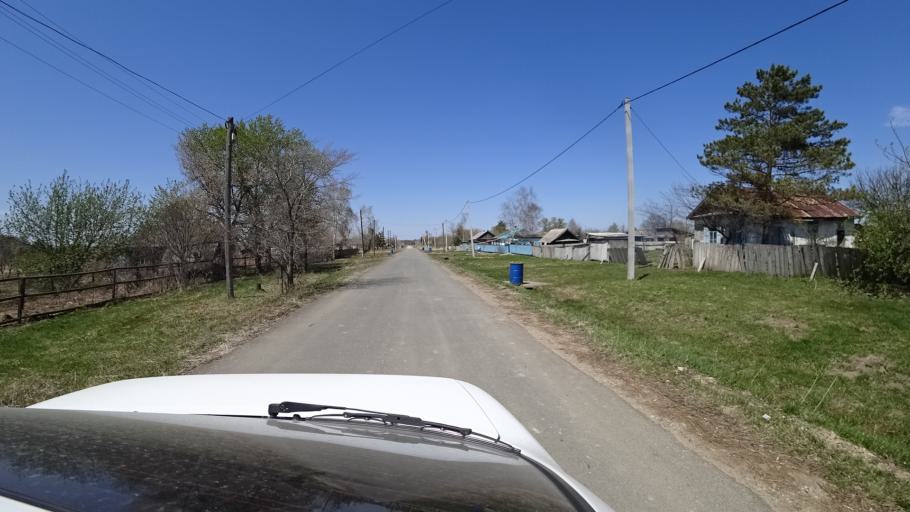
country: RU
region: Primorskiy
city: Dal'nerechensk
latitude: 45.7959
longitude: 133.7708
